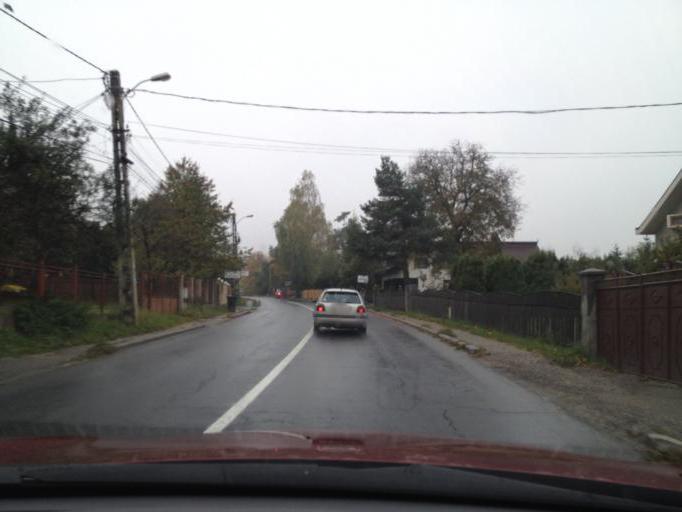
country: RO
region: Brasov
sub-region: Comuna Bran
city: Bran
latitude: 45.5208
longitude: 25.3703
